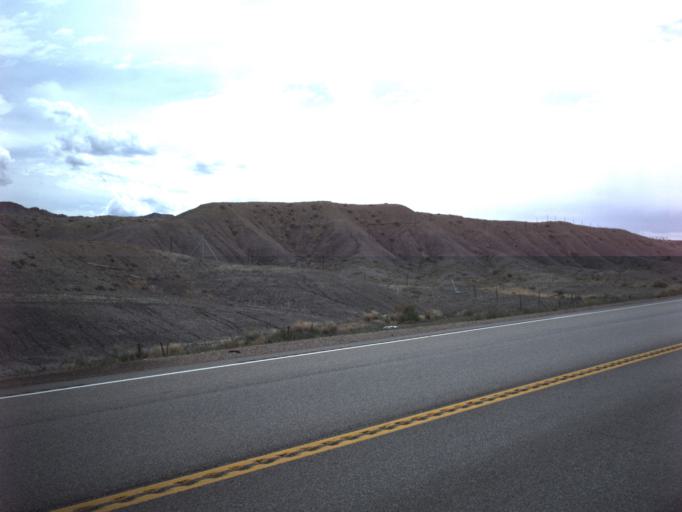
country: US
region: Utah
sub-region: Carbon County
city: East Carbon City
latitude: 39.3069
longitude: -110.3595
